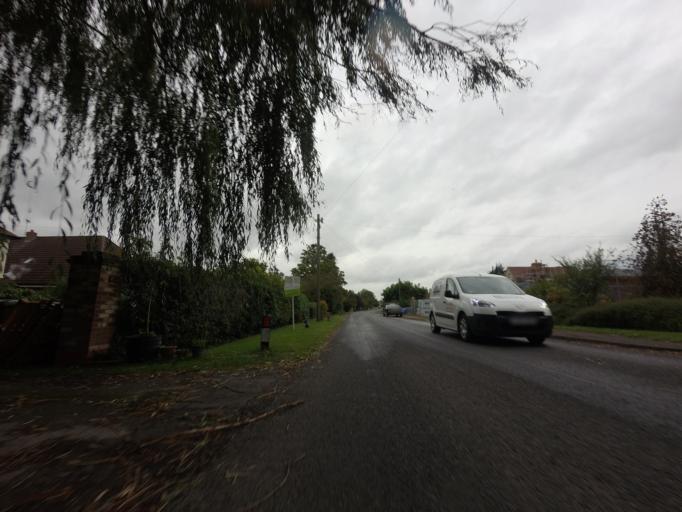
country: GB
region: England
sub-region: Cambridgeshire
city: Comberton
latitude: 52.1548
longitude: 0.0100
